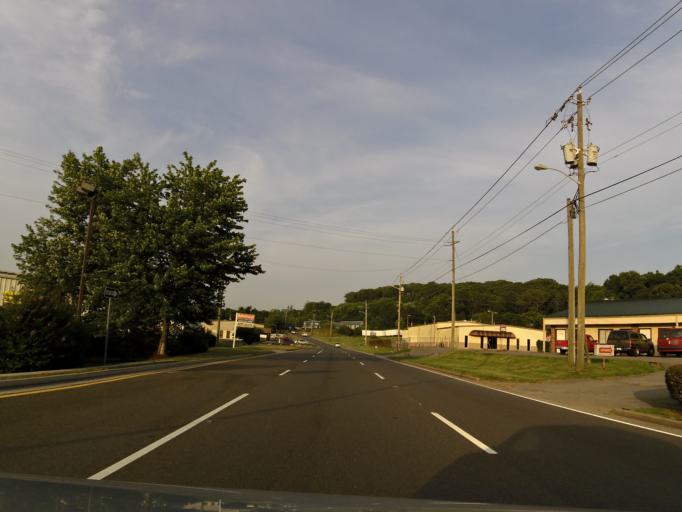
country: US
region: Tennessee
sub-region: Knox County
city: Knoxville
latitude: 35.9566
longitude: -84.0033
